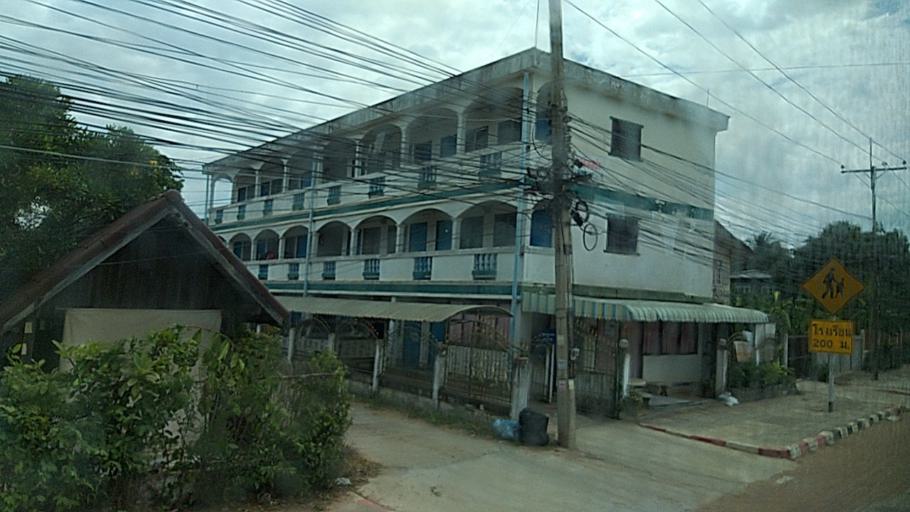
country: TH
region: Maha Sarakham
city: Maha Sarakham
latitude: 16.2387
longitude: 103.2705
